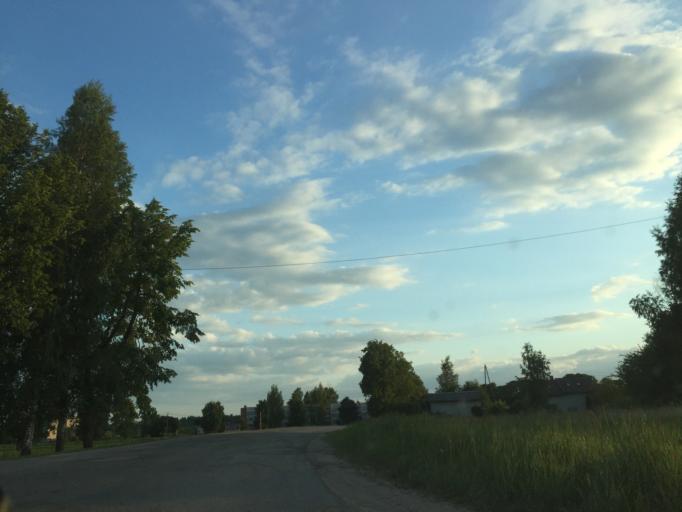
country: LV
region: Sigulda
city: Sigulda
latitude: 57.1103
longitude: 24.9384
